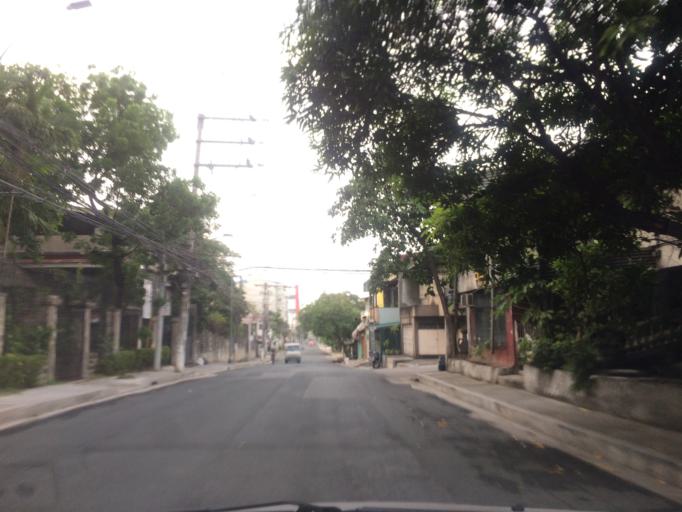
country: PH
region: Calabarzon
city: Del Monte
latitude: 14.6384
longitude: 121.0034
